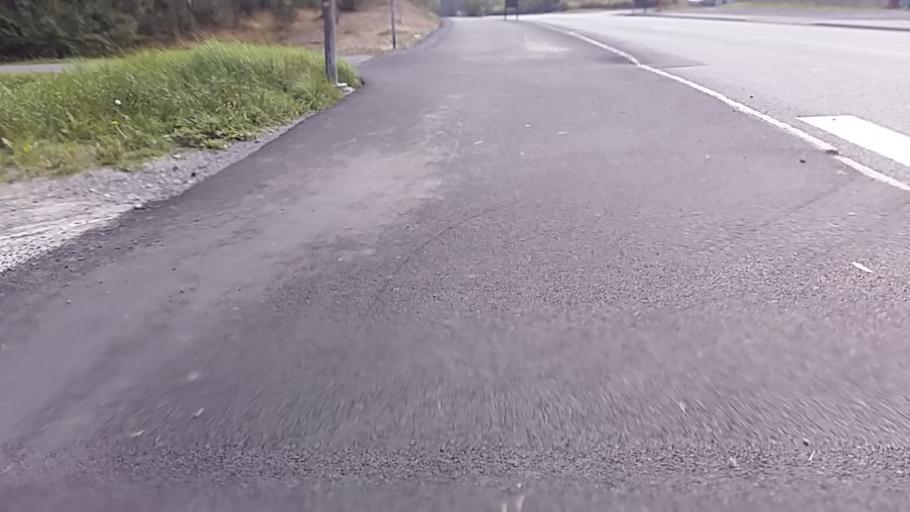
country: SE
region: Joenkoeping
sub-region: Jonkopings Kommun
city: Jonkoping
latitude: 57.7526
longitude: 14.1541
